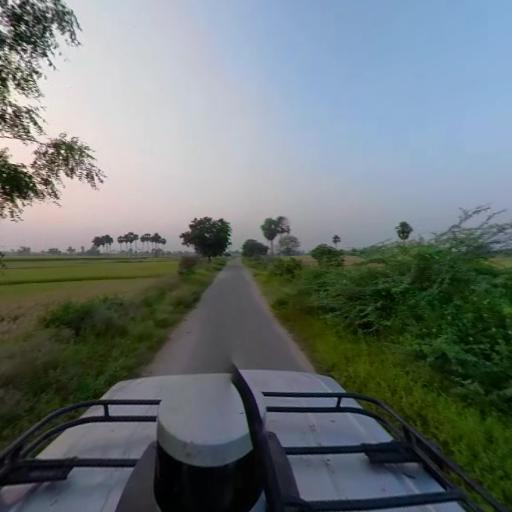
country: IN
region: Telangana
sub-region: Nalgonda
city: Suriapet
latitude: 17.0736
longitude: 79.5483
